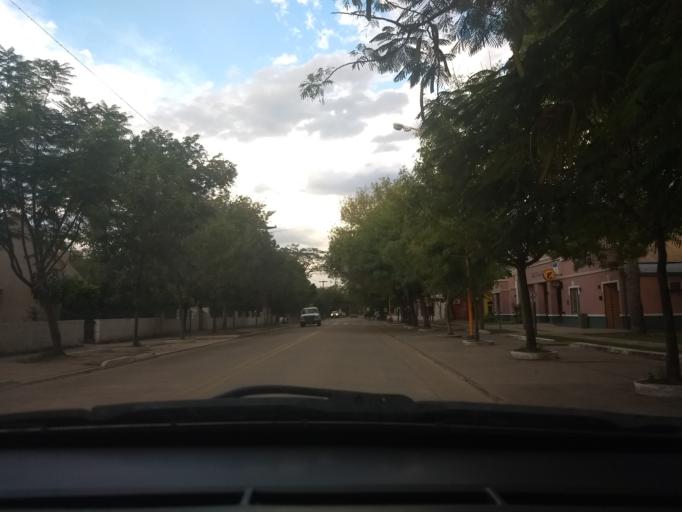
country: AR
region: Corrientes
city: Riachuelo
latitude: -27.5818
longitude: -58.7457
